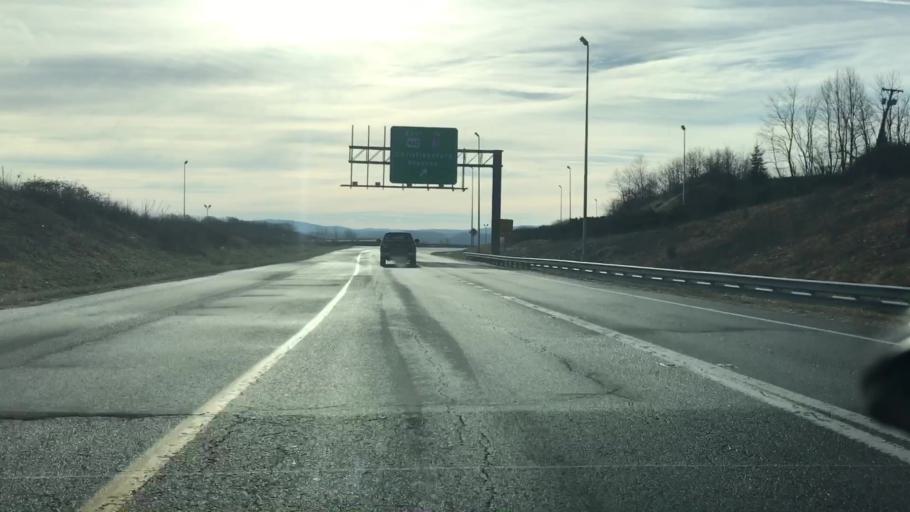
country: US
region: Virginia
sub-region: Montgomery County
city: Merrimac
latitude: 37.1908
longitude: -80.4023
